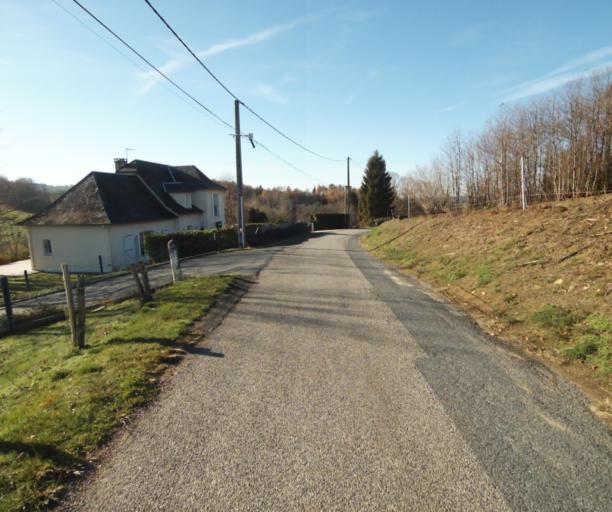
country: FR
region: Limousin
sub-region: Departement de la Correze
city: Sainte-Fortunade
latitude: 45.2247
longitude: 1.7638
